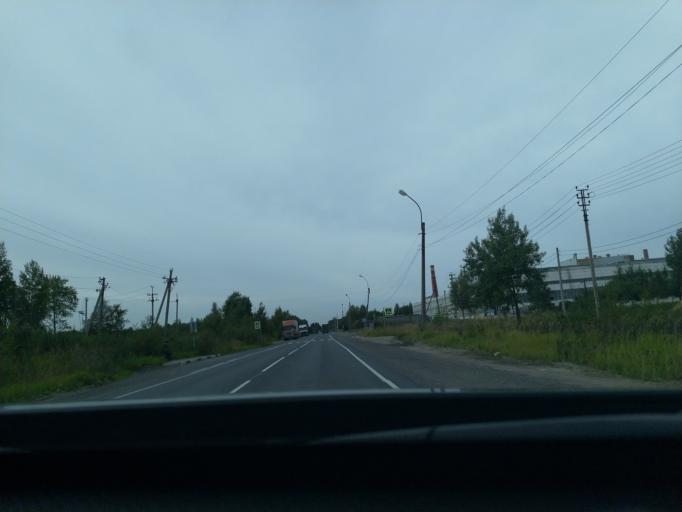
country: RU
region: Leningrad
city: Nikol'skoye
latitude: 59.7260
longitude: 30.7779
